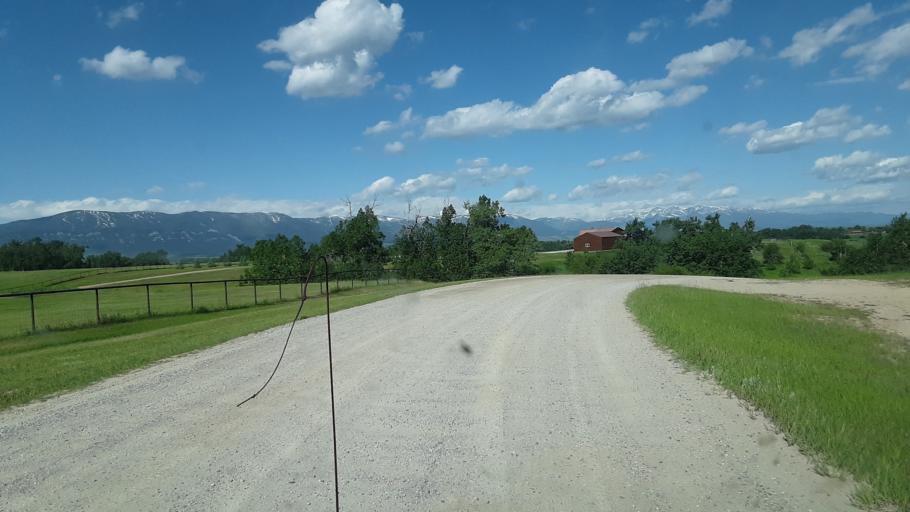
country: US
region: Montana
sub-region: Carbon County
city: Red Lodge
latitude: 45.2781
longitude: -109.2014
